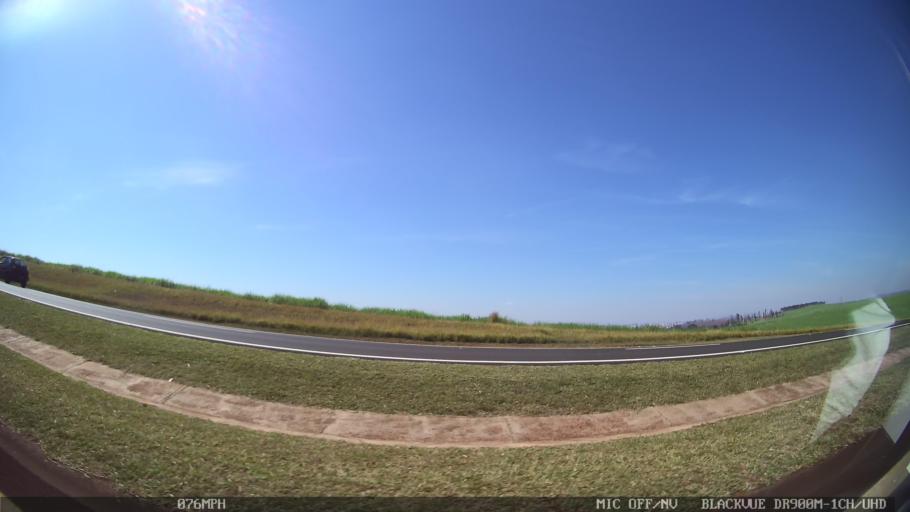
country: BR
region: Sao Paulo
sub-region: Ribeirao Preto
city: Ribeirao Preto
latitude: -21.1755
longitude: -47.8956
